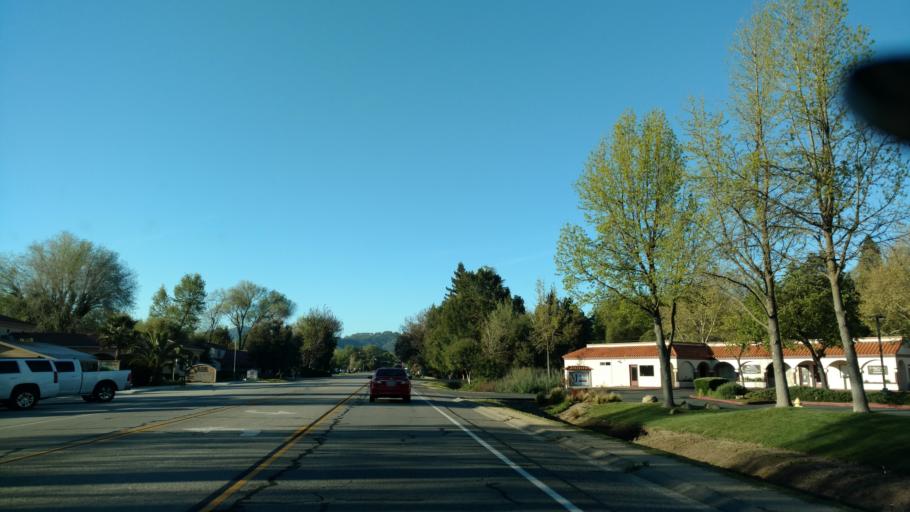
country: US
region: California
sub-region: San Luis Obispo County
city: Atascadero
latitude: 35.4725
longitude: -120.6688
